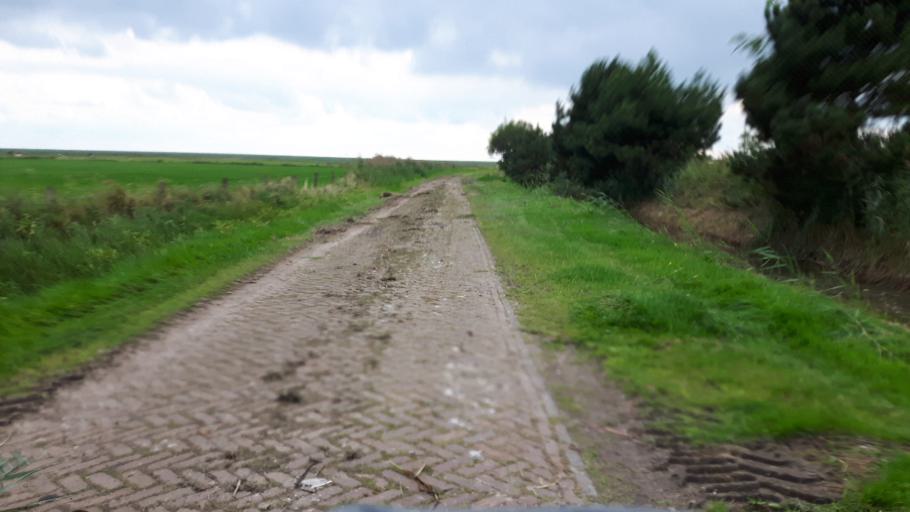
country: NL
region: Friesland
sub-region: Gemeente Ameland
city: Nes
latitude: 53.4492
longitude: 5.8189
